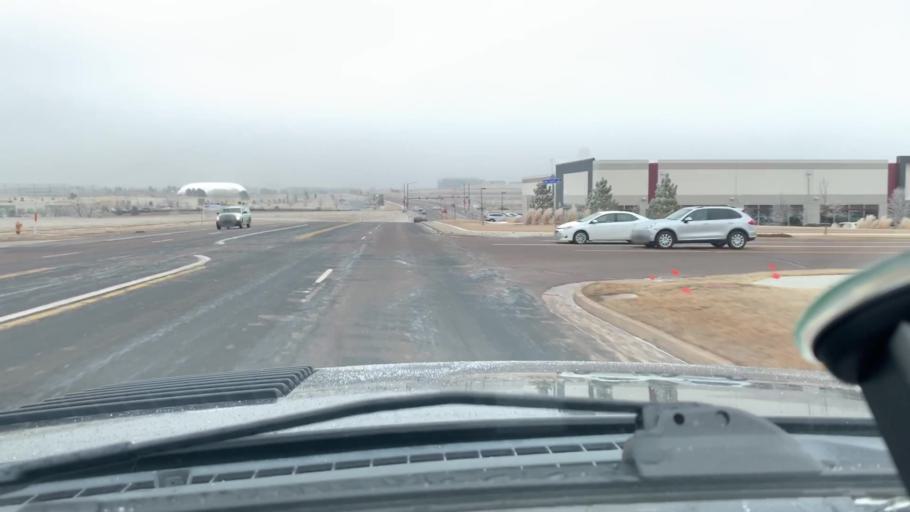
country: US
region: Colorado
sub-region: Arapahoe County
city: Centennial
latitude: 39.5877
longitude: -104.8617
